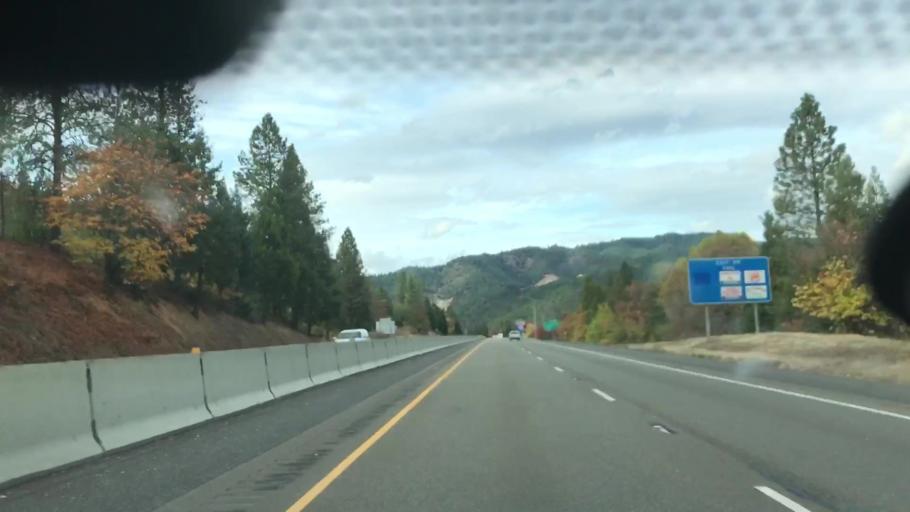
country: US
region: Oregon
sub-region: Douglas County
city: Canyonville
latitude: 42.9308
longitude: -123.2831
